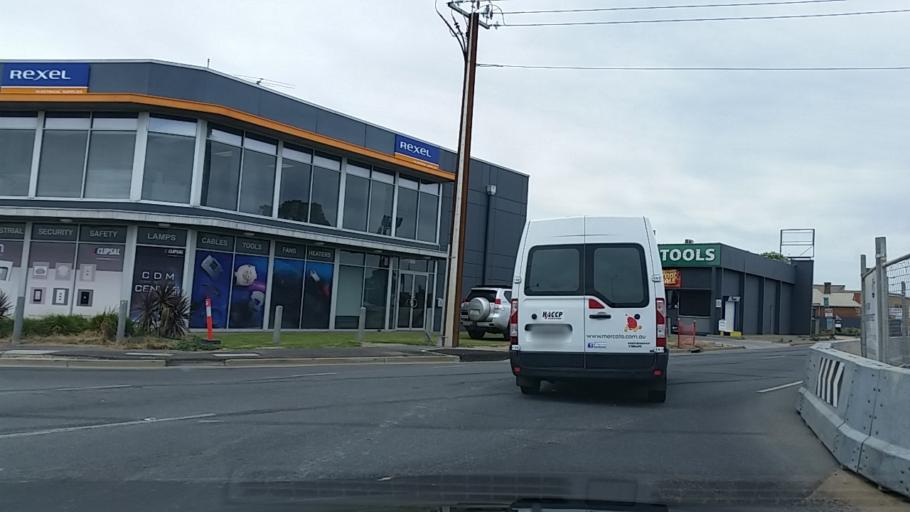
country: AU
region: South Australia
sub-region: City of West Torrens
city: Thebarton
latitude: -34.9046
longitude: 138.5658
